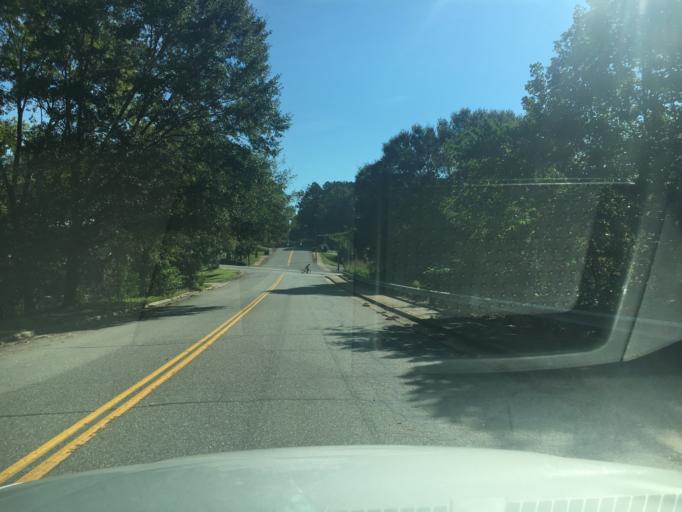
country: US
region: North Carolina
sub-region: Catawba County
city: Hickory
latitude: 35.7241
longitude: -81.3554
